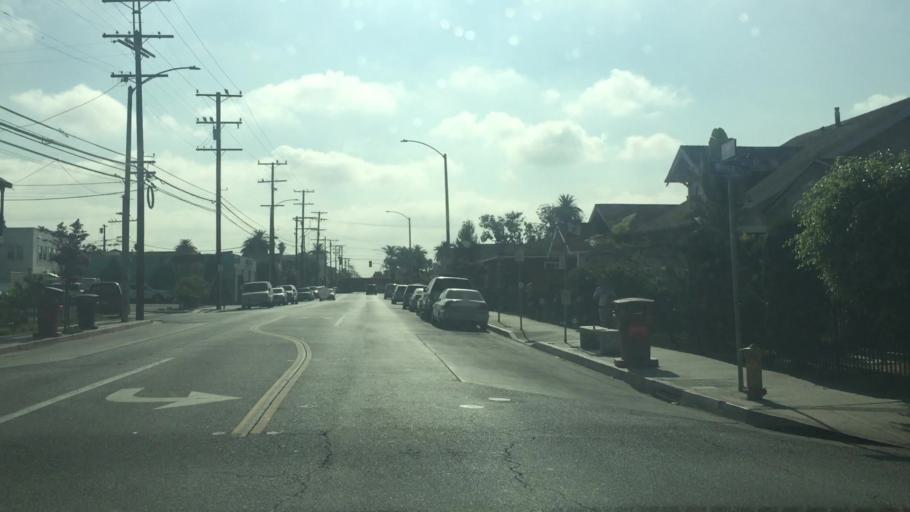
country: US
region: California
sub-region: Los Angeles County
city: Long Beach
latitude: 33.7790
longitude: -118.1698
